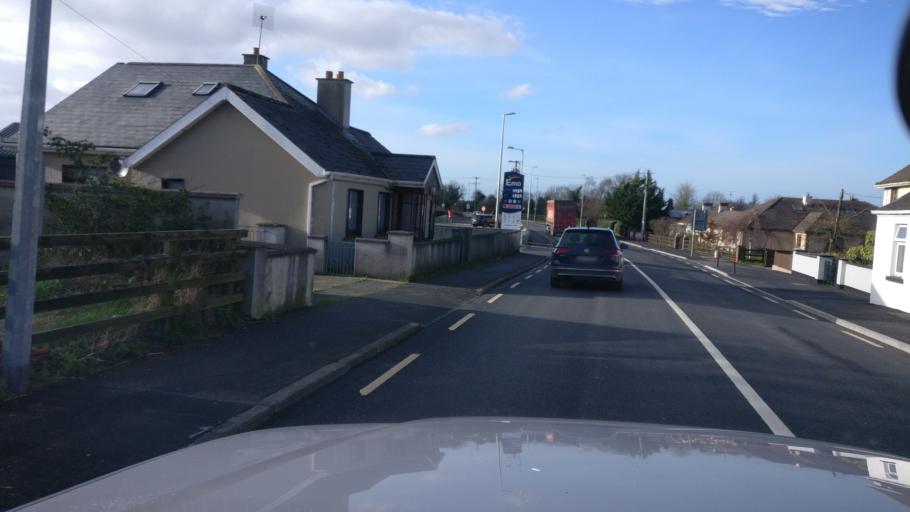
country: IE
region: Leinster
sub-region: Laois
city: Mountmellick
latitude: 53.1233
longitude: -7.3316
